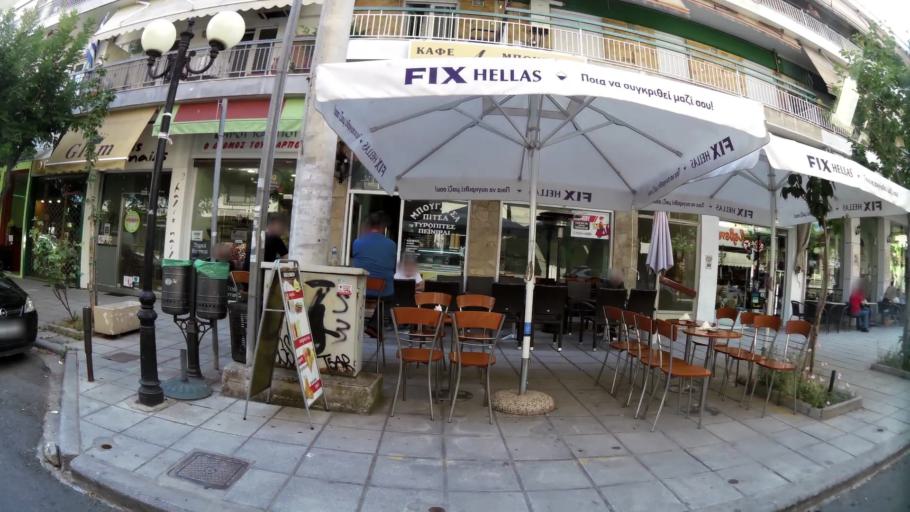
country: GR
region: Central Macedonia
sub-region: Nomos Thessalonikis
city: Kalamaria
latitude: 40.5710
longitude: 22.9584
